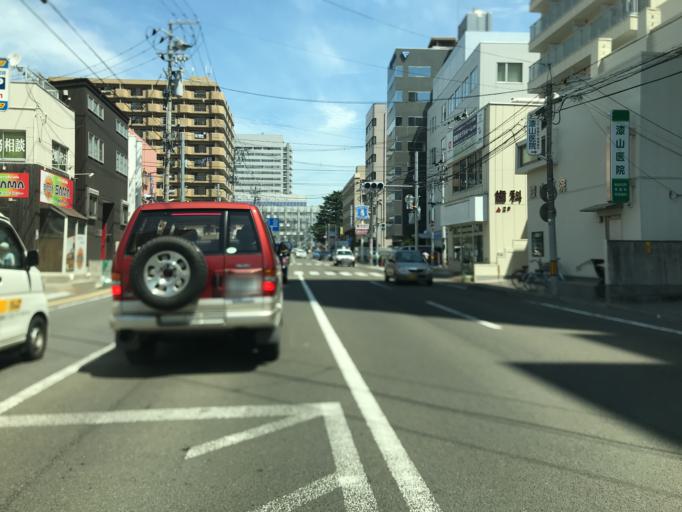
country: JP
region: Miyagi
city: Sendai-shi
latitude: 38.2693
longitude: 140.8622
